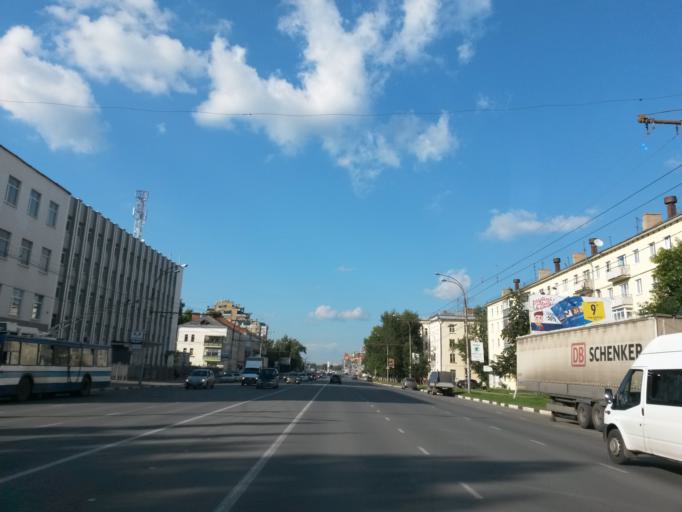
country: RU
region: Ivanovo
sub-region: Gorod Ivanovo
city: Ivanovo
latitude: 56.9774
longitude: 40.9766
